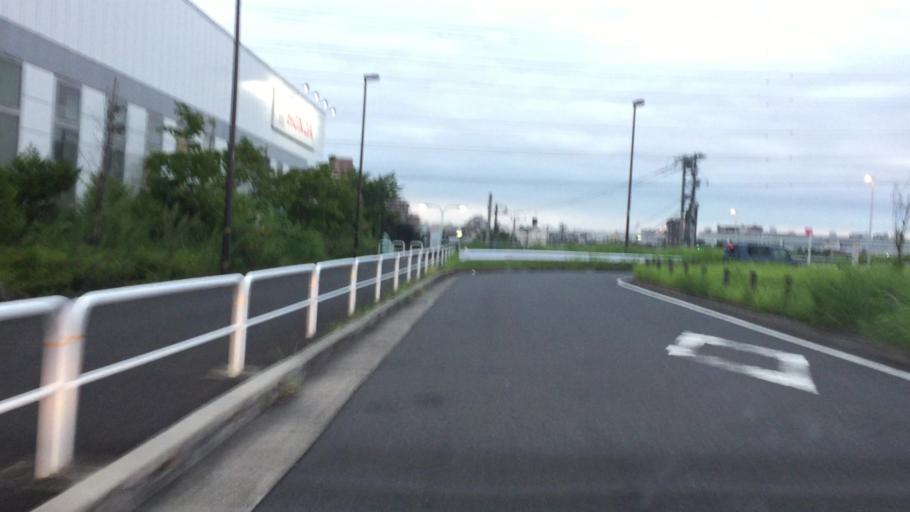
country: JP
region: Saitama
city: Soka
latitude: 35.7560
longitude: 139.7676
